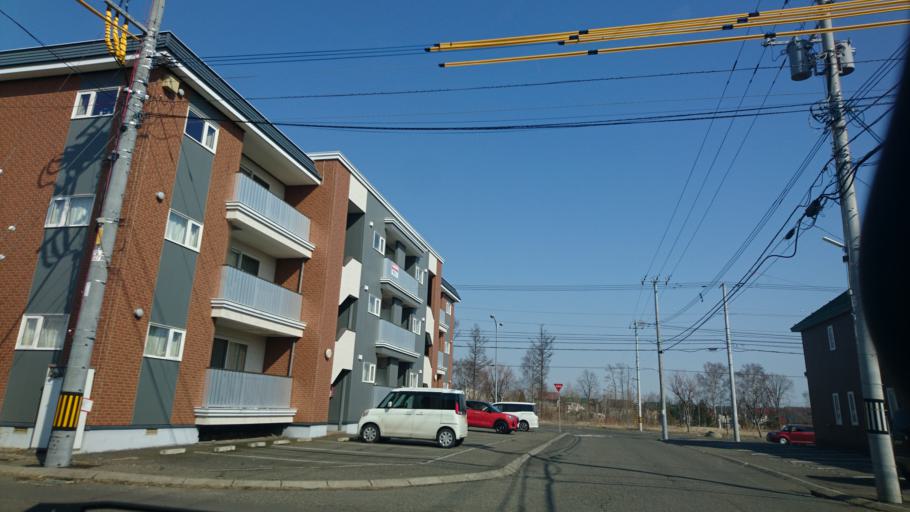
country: JP
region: Hokkaido
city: Obihiro
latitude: 42.9151
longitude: 143.1144
